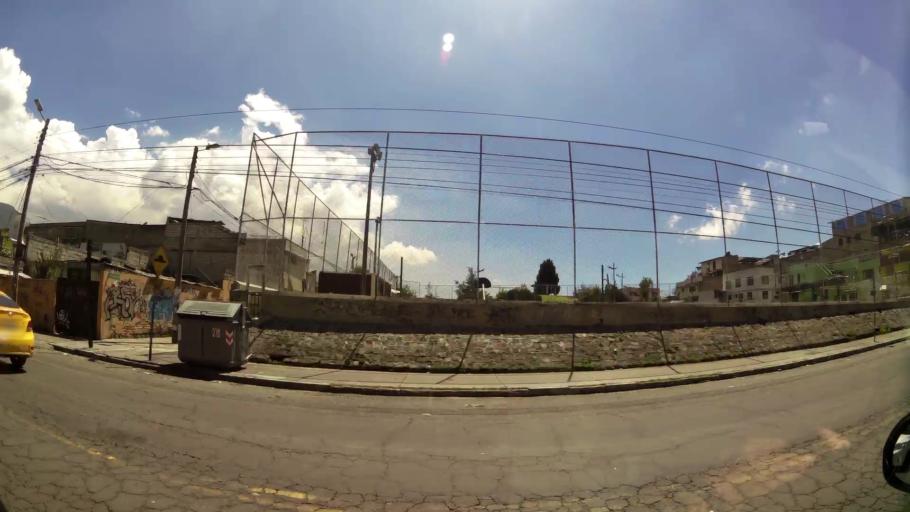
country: EC
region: Pichincha
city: Quito
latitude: -0.2692
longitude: -78.5298
